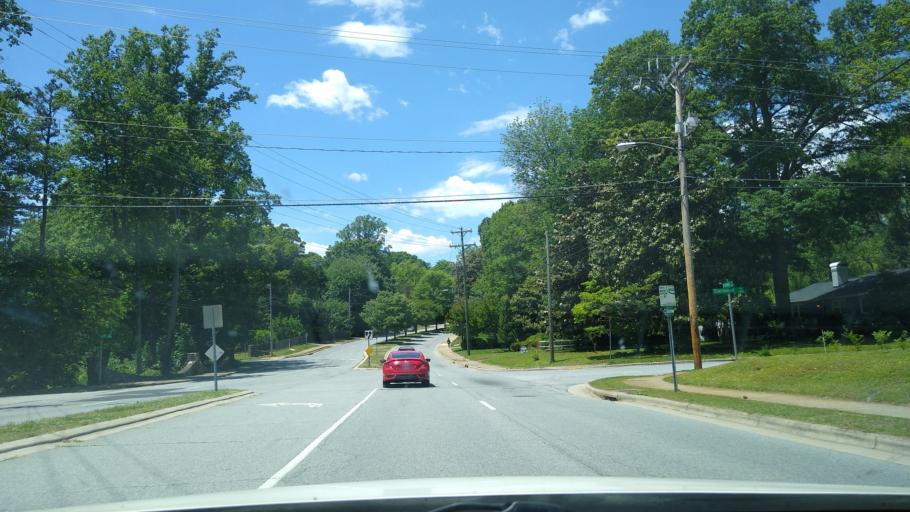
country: US
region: North Carolina
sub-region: Guilford County
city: Greensboro
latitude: 36.0913
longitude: -79.8645
